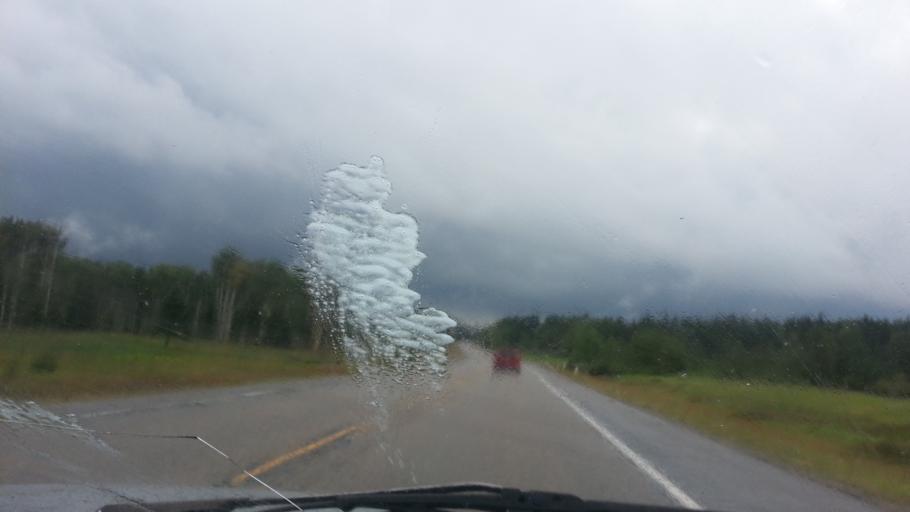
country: CA
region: Alberta
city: Cochrane
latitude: 50.9214
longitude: -114.5806
